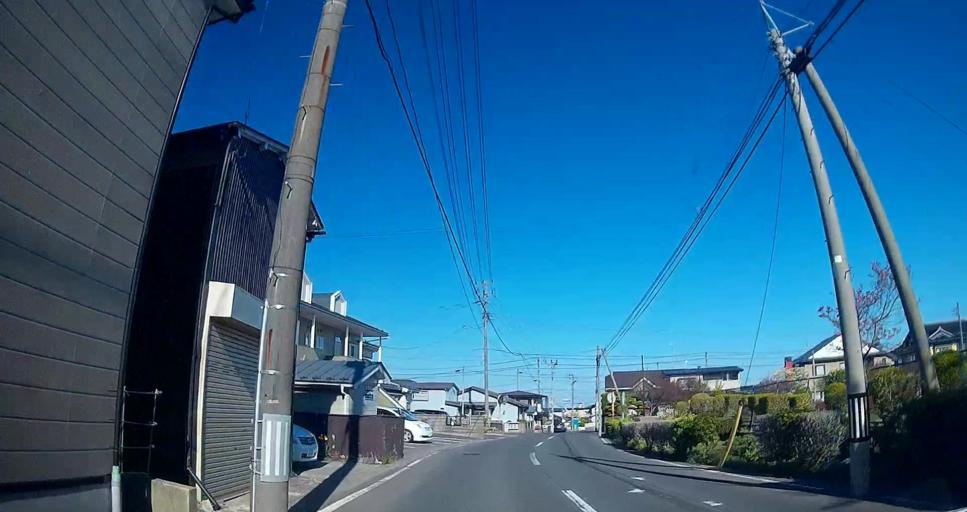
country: JP
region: Aomori
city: Hachinohe
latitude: 40.5245
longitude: 141.5517
